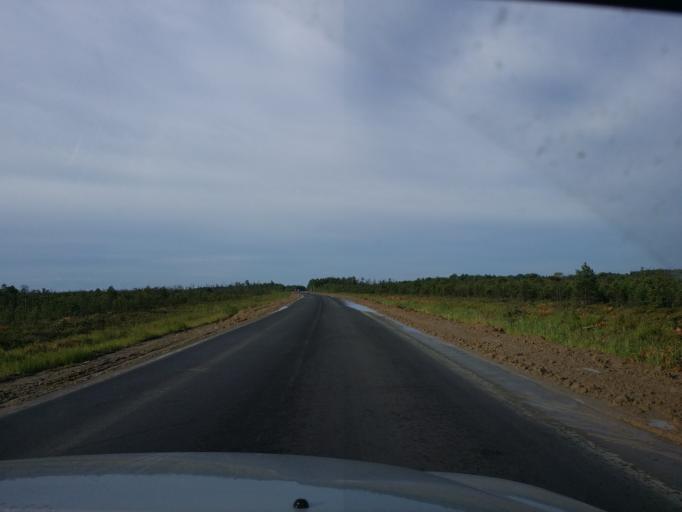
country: RU
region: Tjumen
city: Uvat
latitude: 59.3579
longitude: 68.9796
